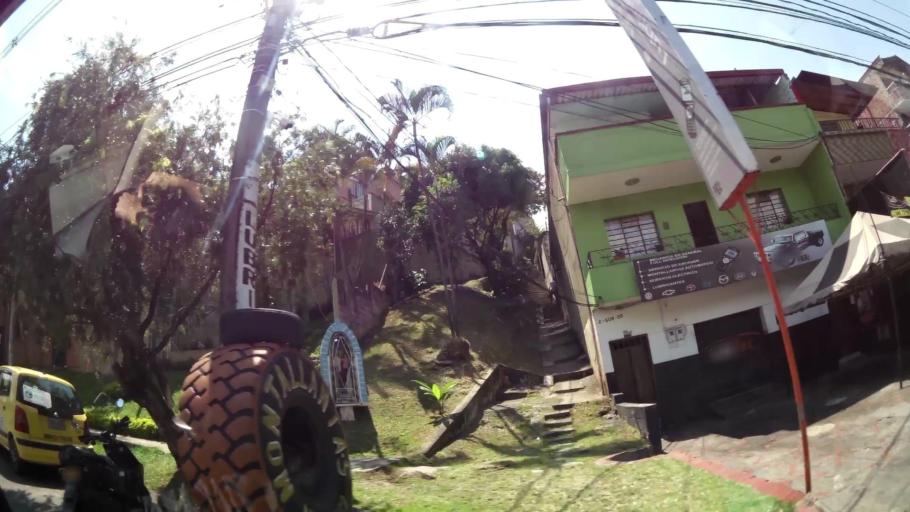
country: CO
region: Antioquia
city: Itagui
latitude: 6.2091
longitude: -75.6014
